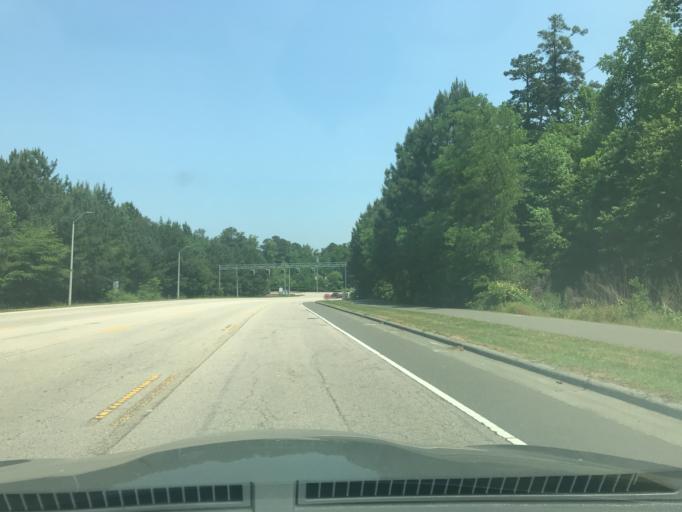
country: US
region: North Carolina
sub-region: Wake County
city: Cary
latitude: 35.8024
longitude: -78.7267
